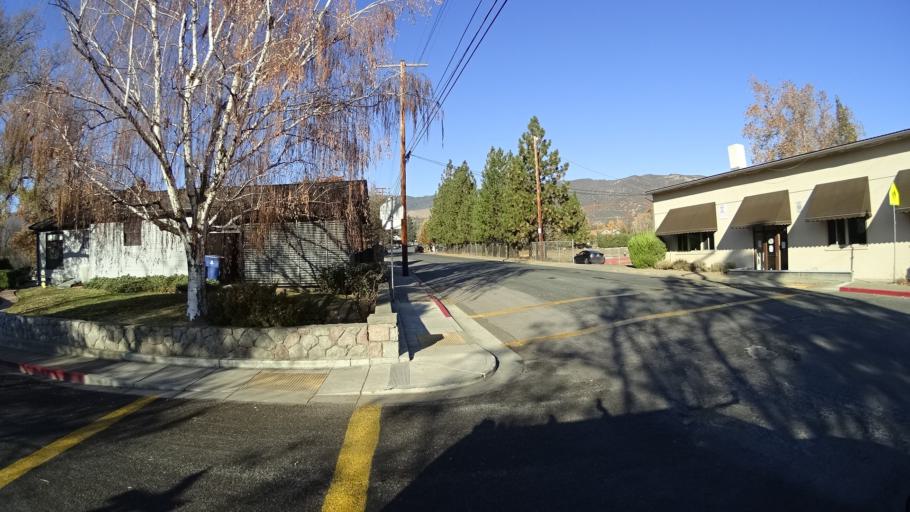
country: US
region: California
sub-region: Siskiyou County
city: Yreka
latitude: 41.7369
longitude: -122.6384
